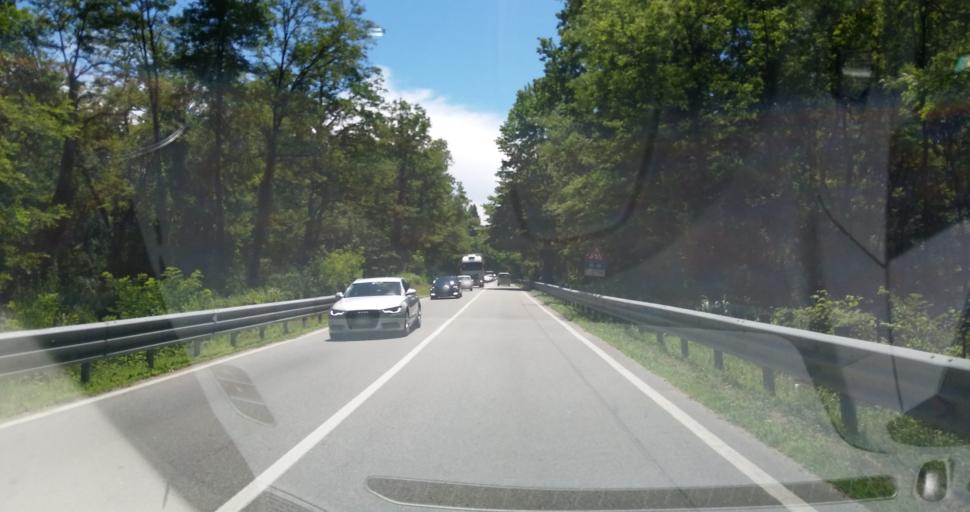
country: IT
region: Lombardy
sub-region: Provincia di Varese
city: Vergiate
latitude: 45.7021
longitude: 8.7005
